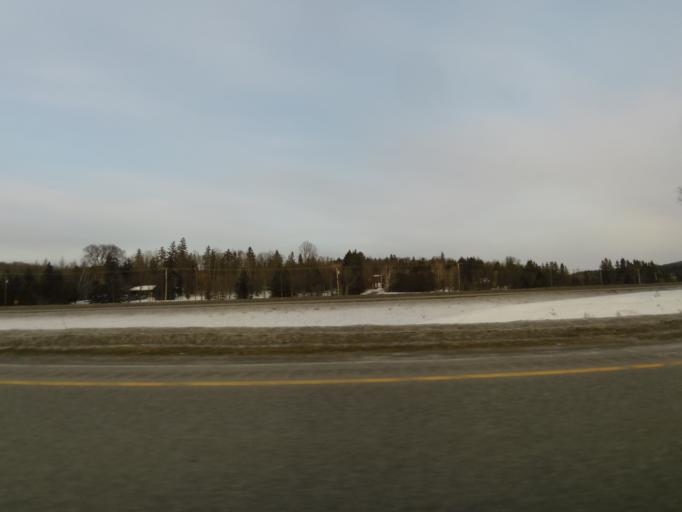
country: CA
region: Quebec
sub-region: Outaouais
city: Wakefield
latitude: 45.5846
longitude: -75.8890
